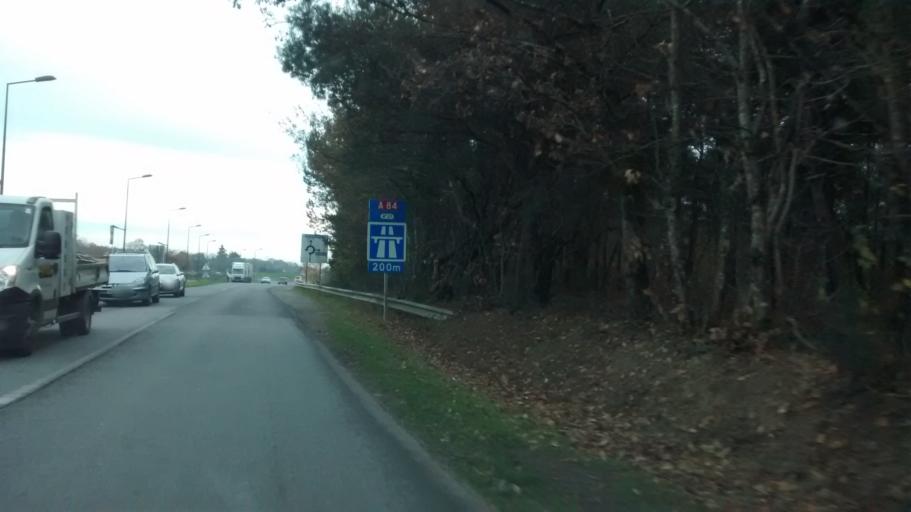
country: FR
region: Brittany
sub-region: Departement d'Ille-et-Vilaine
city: Liffre
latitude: 48.2247
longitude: -1.5022
